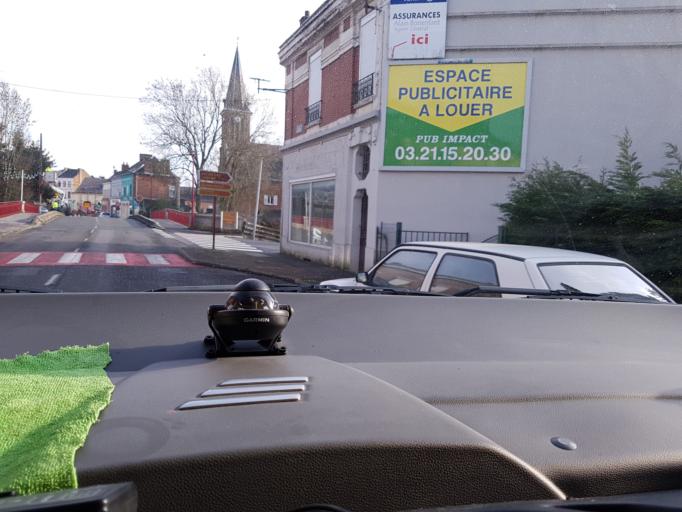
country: FR
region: Picardie
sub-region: Departement de l'Aisne
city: Hirson
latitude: 49.9246
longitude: 4.0778
